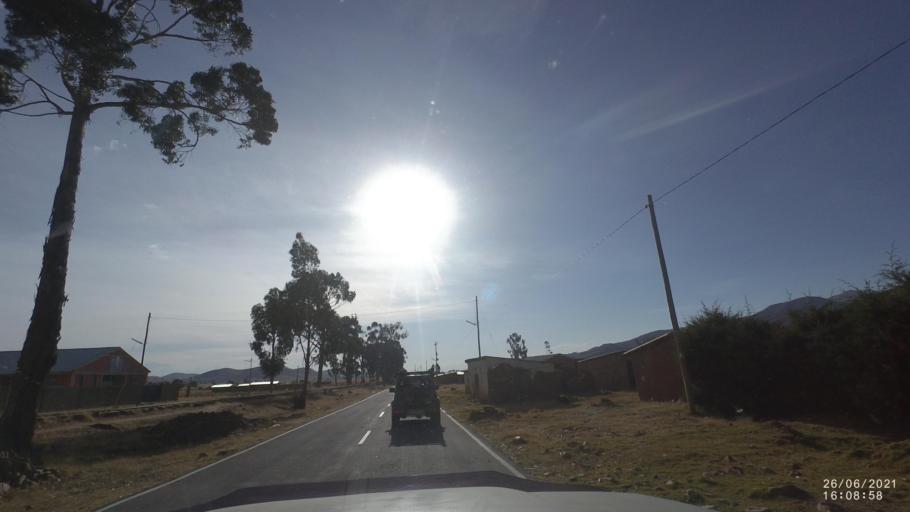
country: BO
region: Cochabamba
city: Arani
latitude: -17.8164
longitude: -65.7807
